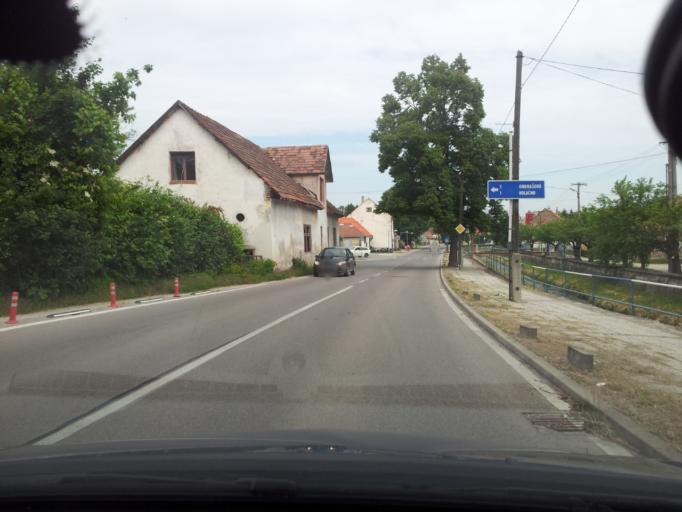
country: SK
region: Nitriansky
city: Partizanske
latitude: 48.6072
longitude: 18.4366
